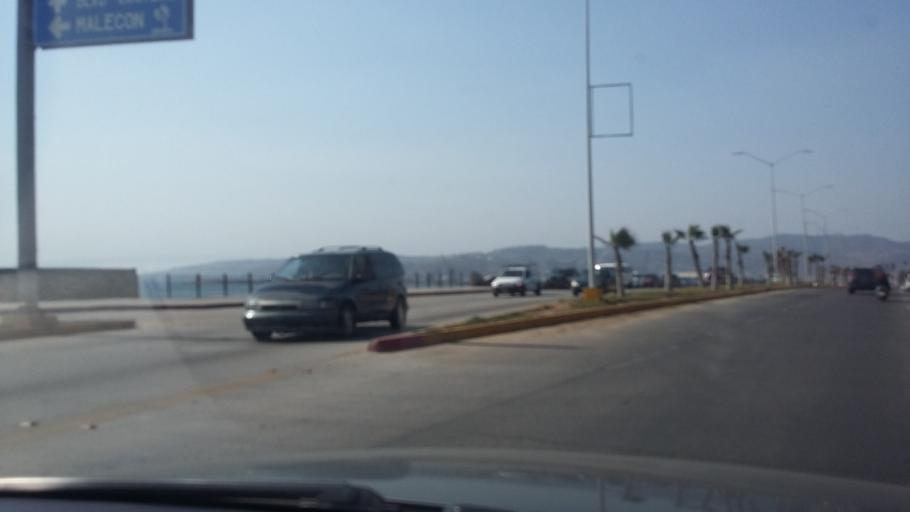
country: MX
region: Baja California
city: Ensenada
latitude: 31.8340
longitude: -116.6096
